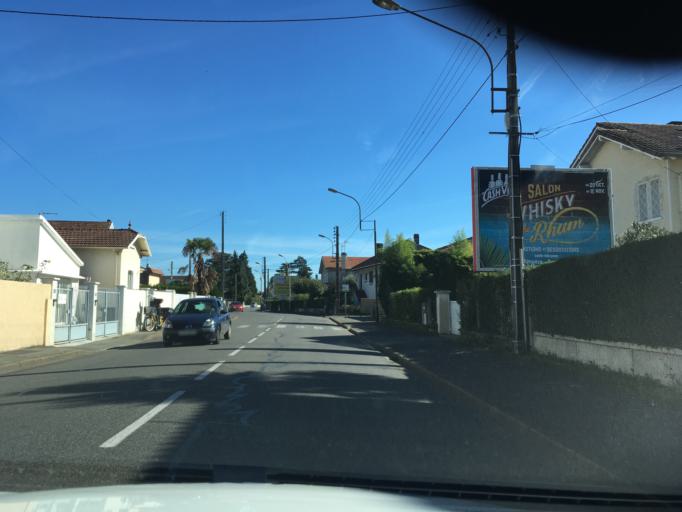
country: FR
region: Aquitaine
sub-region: Departement des Pyrenees-Atlantiques
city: Lons
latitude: 43.3243
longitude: -0.3785
